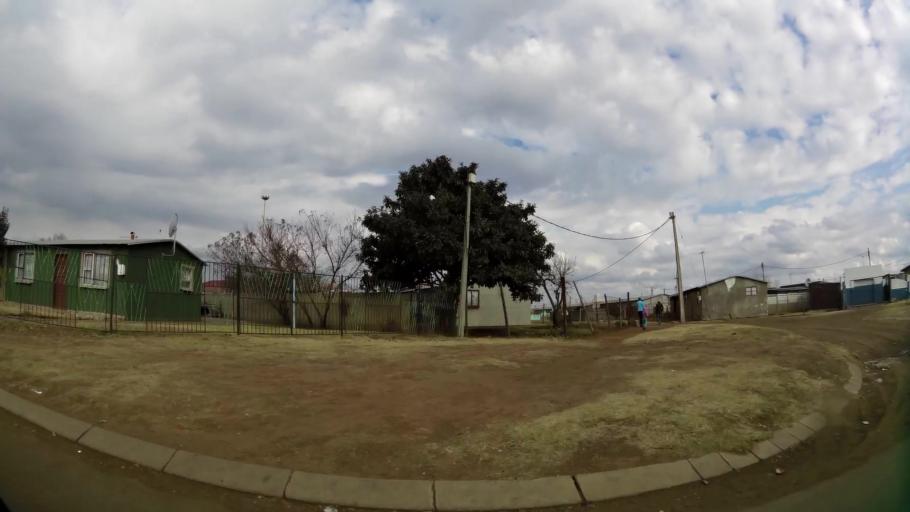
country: ZA
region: Gauteng
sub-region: Sedibeng District Municipality
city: Vanderbijlpark
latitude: -26.6962
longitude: 27.7916
